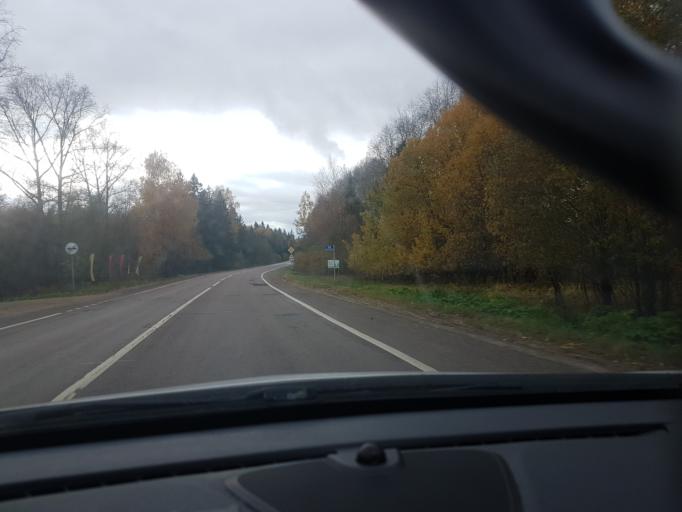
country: RU
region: Moskovskaya
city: Sychevo
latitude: 56.0045
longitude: 36.3215
